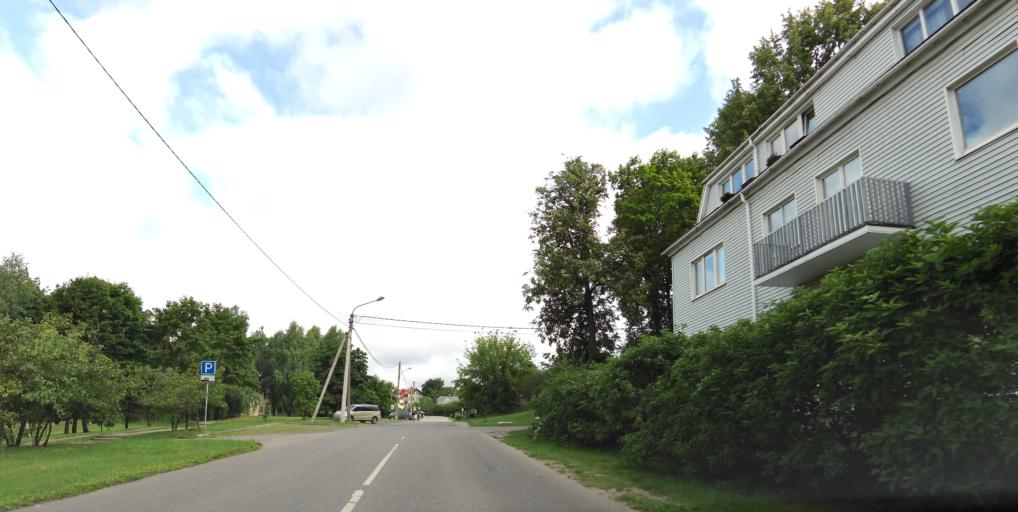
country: LT
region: Vilnius County
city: Seskine
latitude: 54.6909
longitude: 25.2465
